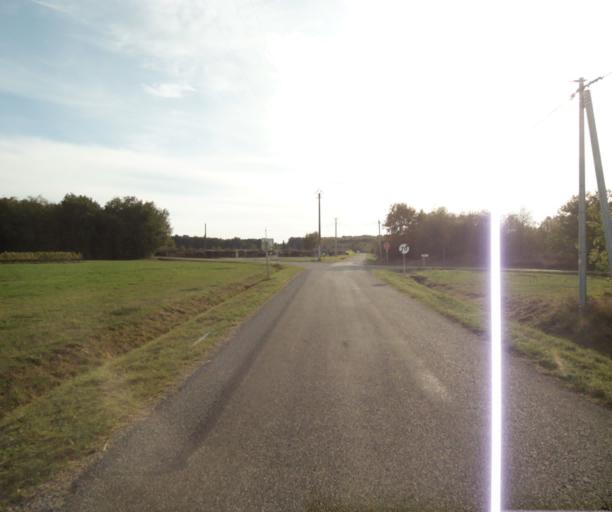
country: FR
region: Midi-Pyrenees
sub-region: Departement du Tarn-et-Garonne
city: Campsas
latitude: 43.8830
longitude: 1.3234
